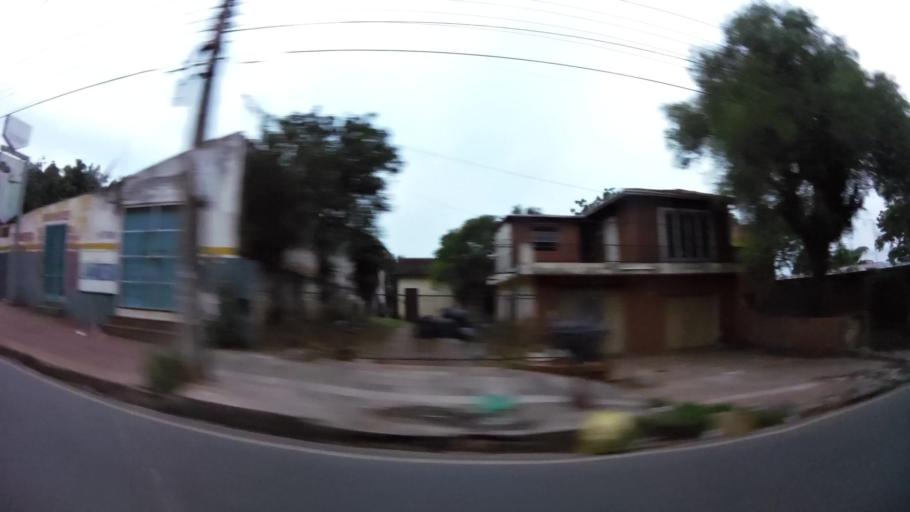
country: PY
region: Central
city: Lambare
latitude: -25.3276
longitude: -57.5984
